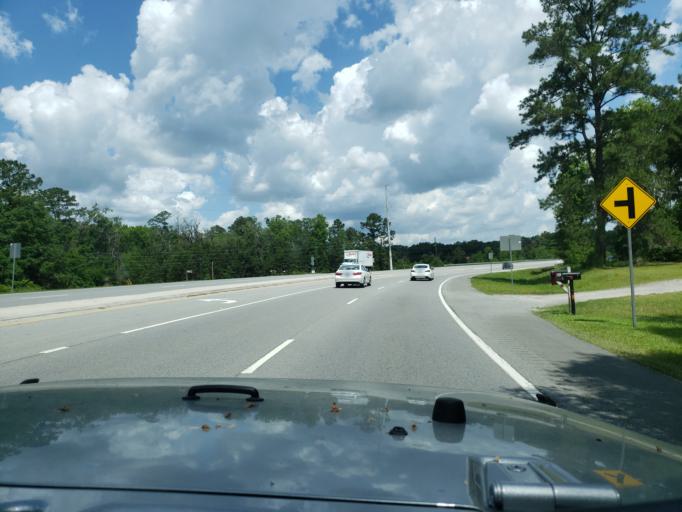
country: US
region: Georgia
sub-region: Chatham County
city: Georgetown
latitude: 32.0463
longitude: -81.2141
